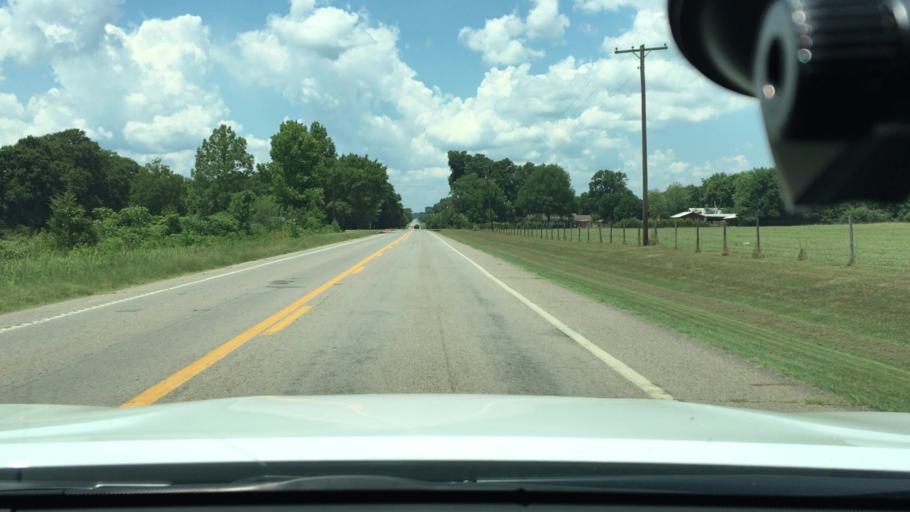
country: US
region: Arkansas
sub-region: Logan County
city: Booneville
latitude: 35.1474
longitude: -93.8427
